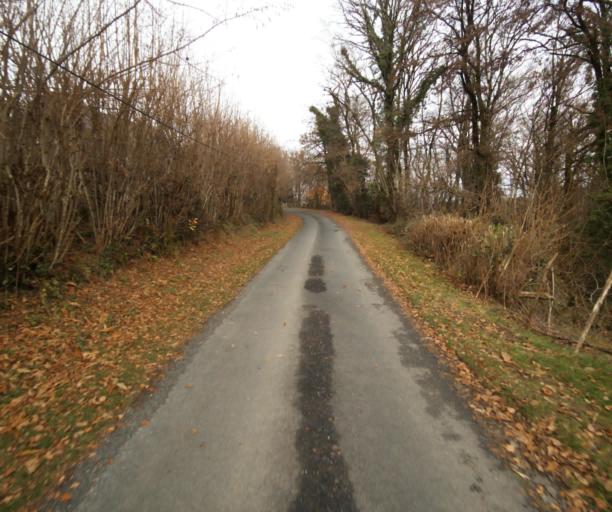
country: FR
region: Limousin
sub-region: Departement de la Correze
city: Saint-Mexant
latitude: 45.2624
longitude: 1.6501
